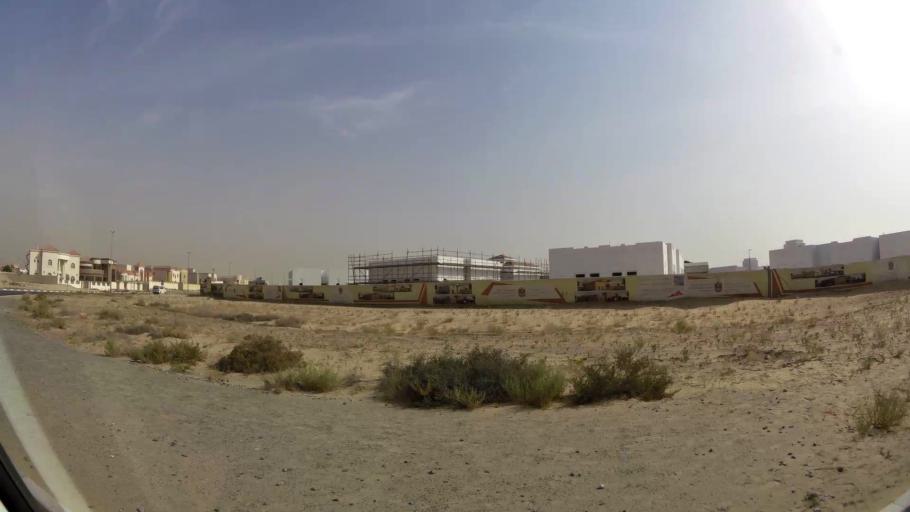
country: AE
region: Ash Shariqah
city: Sharjah
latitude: 25.2638
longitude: 55.4567
